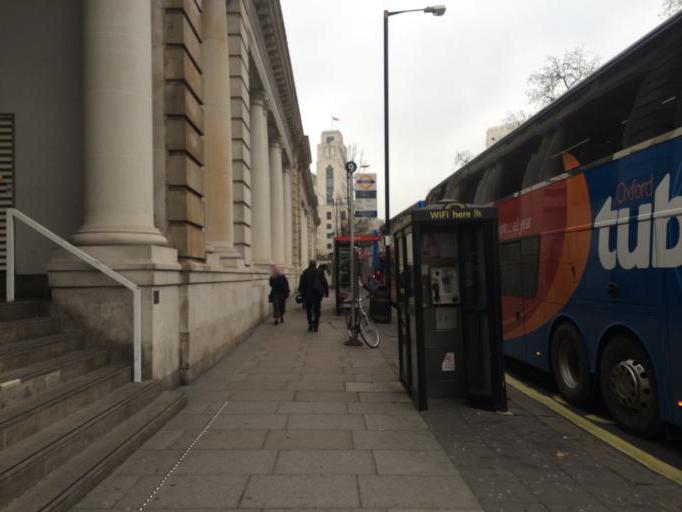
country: GB
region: England
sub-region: Greater London
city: Battersea
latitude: 51.4933
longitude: -0.1472
